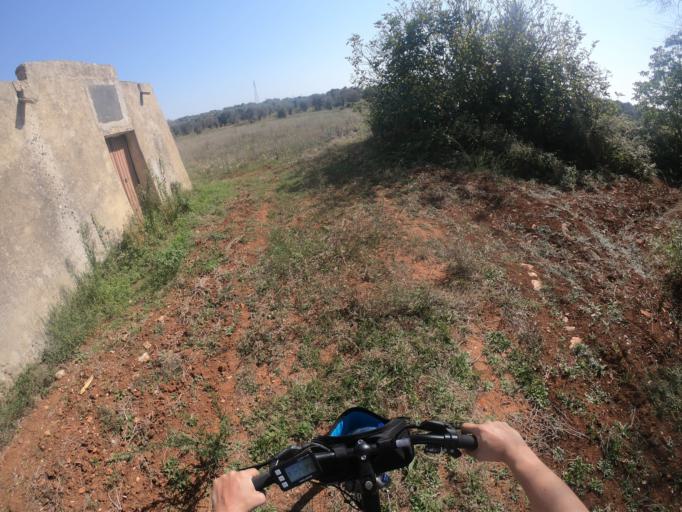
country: IT
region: Apulia
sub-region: Provincia di Lecce
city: Specchia
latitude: 39.9153
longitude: 18.2858
